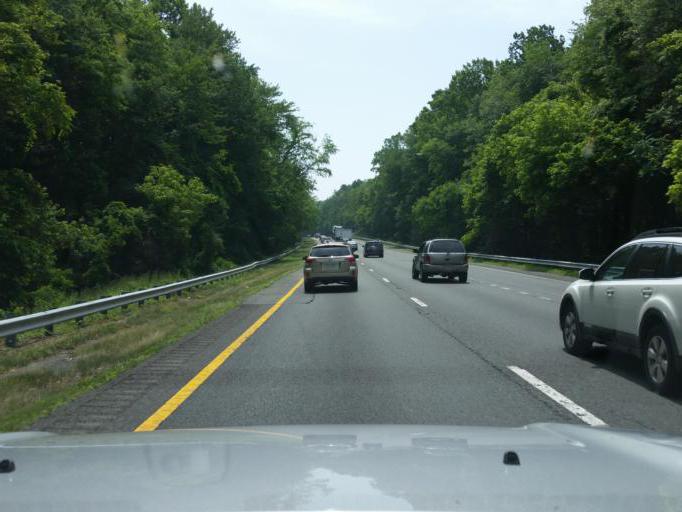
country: US
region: Maryland
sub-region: Montgomery County
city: Clarksburg
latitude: 39.2595
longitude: -77.3083
